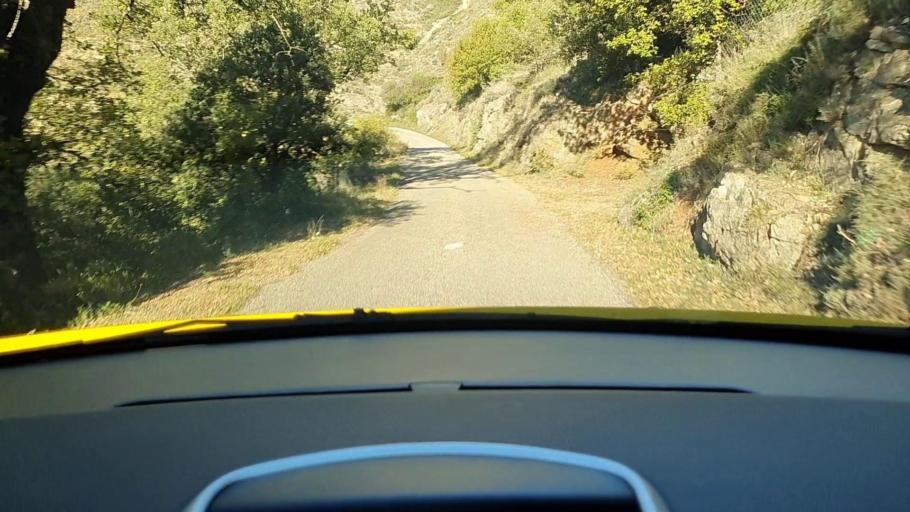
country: FR
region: Languedoc-Roussillon
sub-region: Departement du Gard
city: Sumene
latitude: 43.9776
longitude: 3.7601
